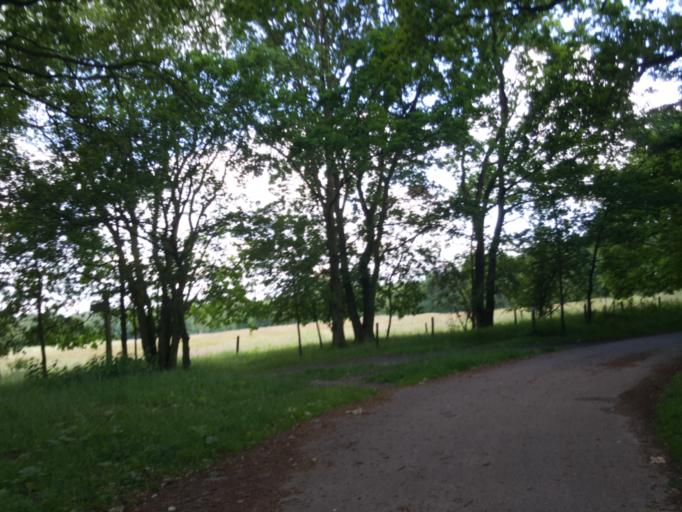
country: DE
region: Schleswig-Holstein
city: Oststeinbek
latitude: 53.5185
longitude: 10.1335
